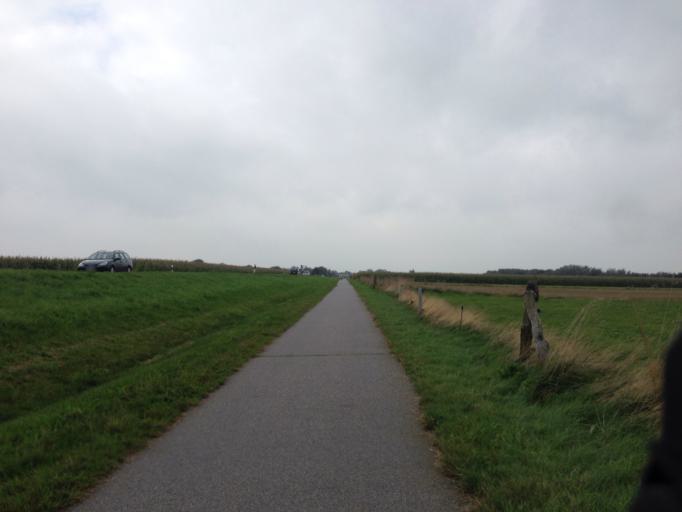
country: DE
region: Schleswig-Holstein
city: Oevenum
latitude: 54.7060
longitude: 8.5255
